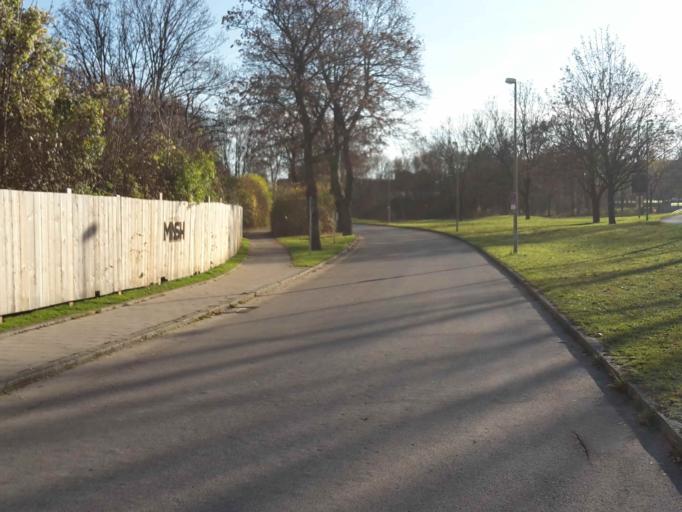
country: DE
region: Bavaria
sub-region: Upper Bavaria
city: Munich
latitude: 48.1701
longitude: 11.5394
